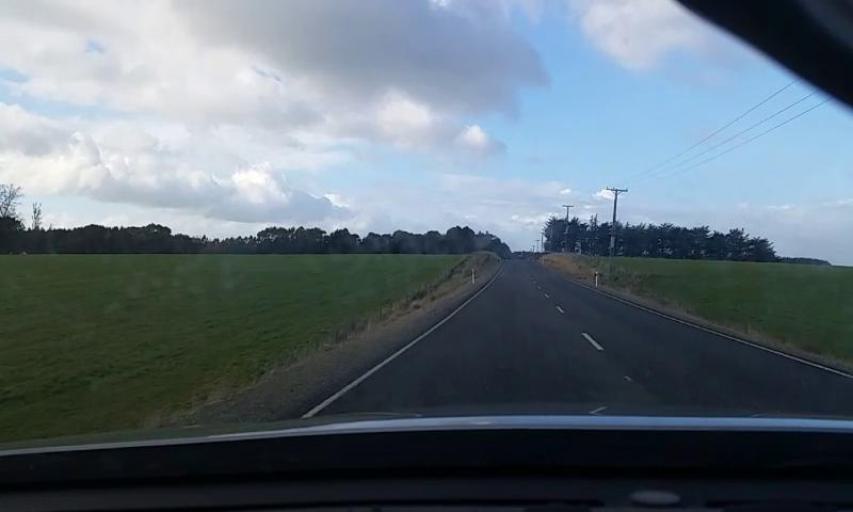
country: NZ
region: Southland
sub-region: Invercargill City
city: Invercargill
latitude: -46.3807
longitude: 168.4249
